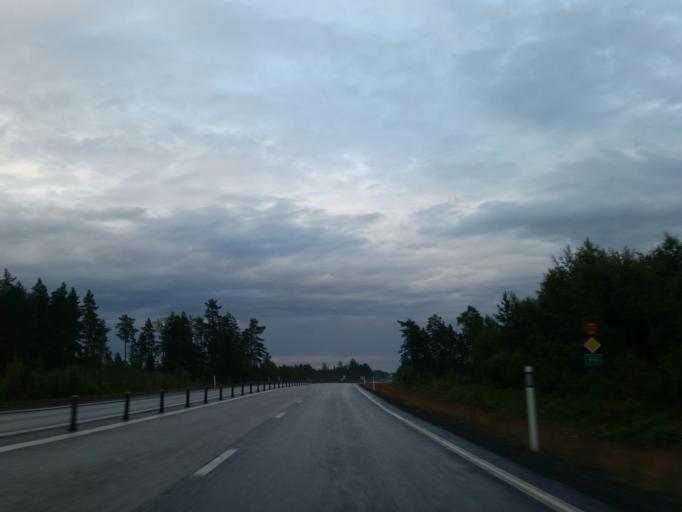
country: SE
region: Vaesterbotten
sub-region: Umea Kommun
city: Saevar
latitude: 63.9564
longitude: 20.6746
